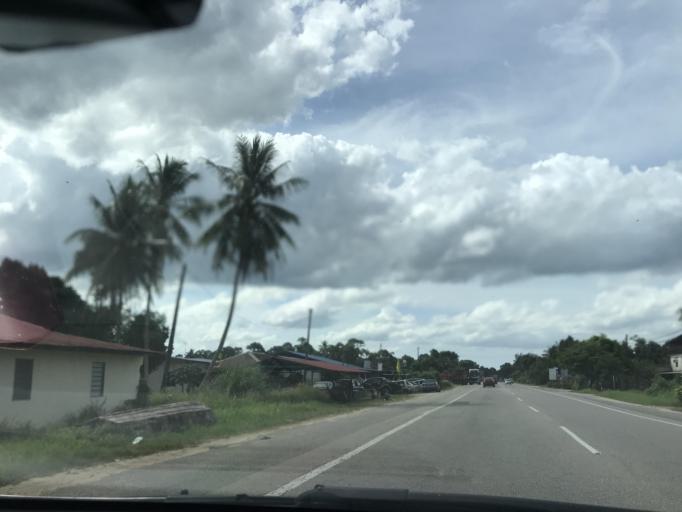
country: MY
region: Kelantan
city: Kampong Pangkal Kalong
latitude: 5.9100
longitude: 102.1875
